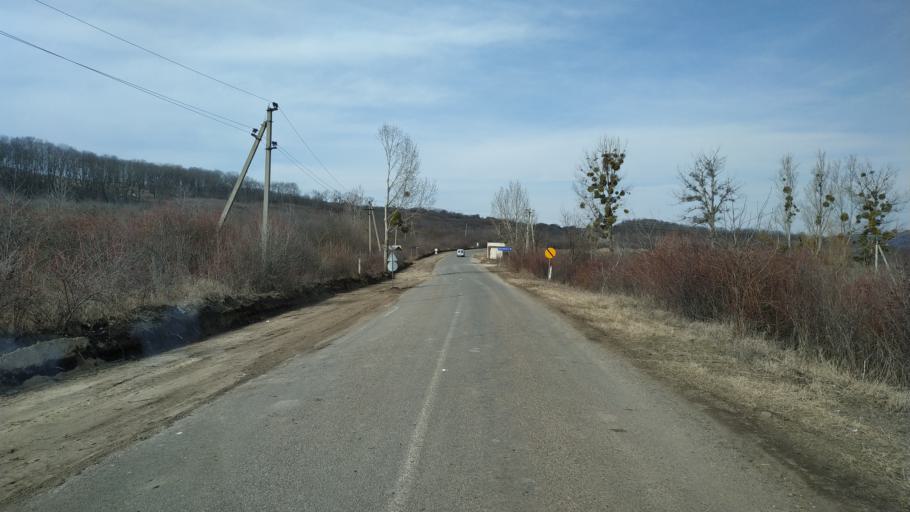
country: MD
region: Nisporeni
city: Nisporeni
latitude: 47.1843
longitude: 28.0746
